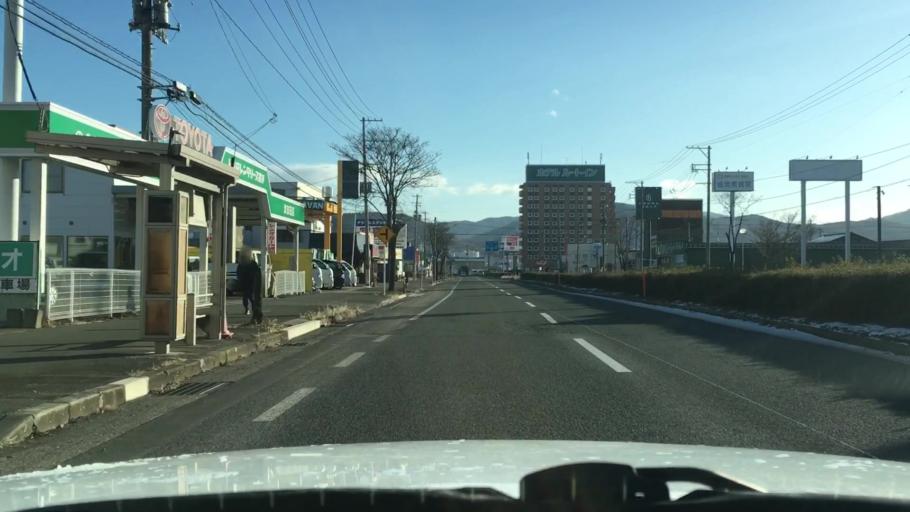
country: JP
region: Iwate
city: Morioka-shi
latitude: 39.6572
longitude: 141.1550
